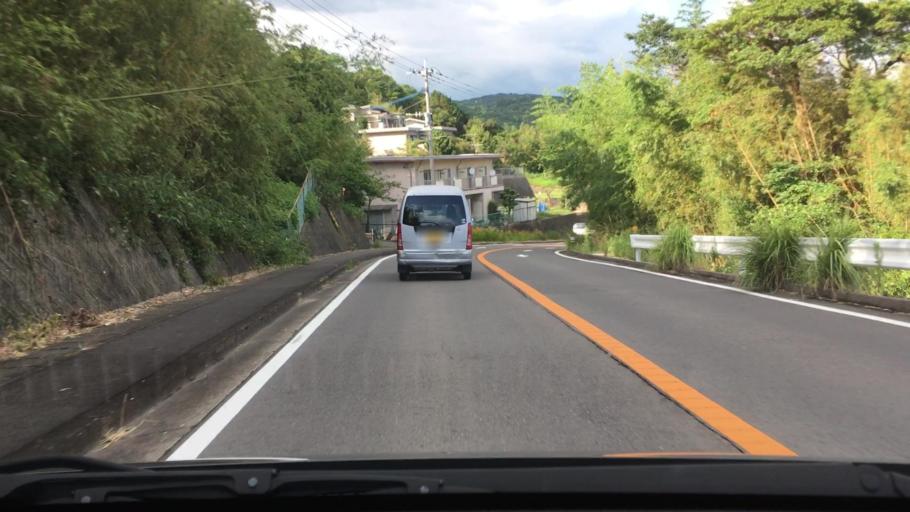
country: JP
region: Nagasaki
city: Togitsu
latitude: 32.8382
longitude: 129.7092
